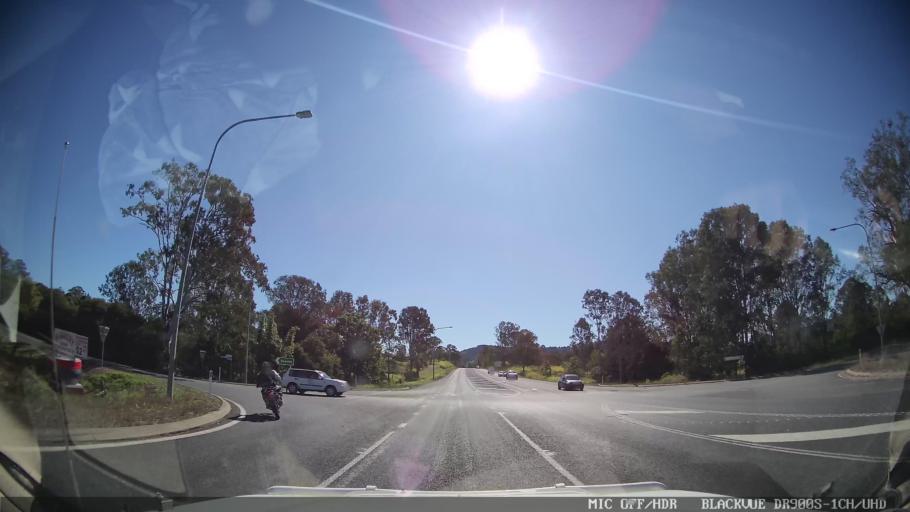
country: AU
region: Queensland
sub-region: Gympie Regional Council
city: Gympie
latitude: -25.9953
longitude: 152.5663
